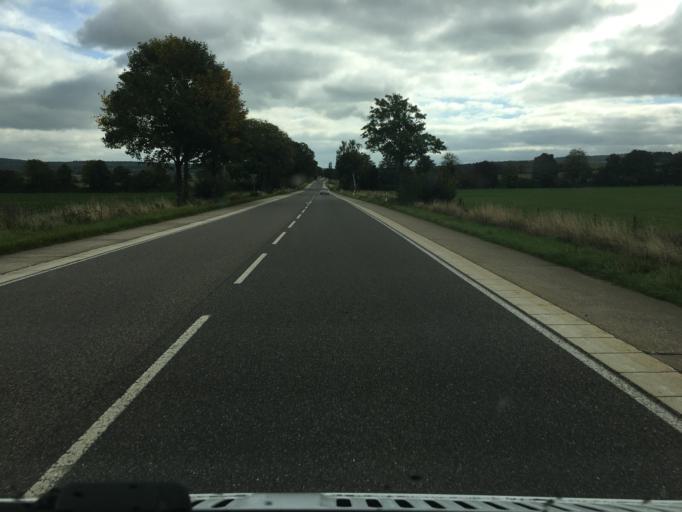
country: DE
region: North Rhine-Westphalia
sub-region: Regierungsbezirk Koln
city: Euskirchen
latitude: 50.6145
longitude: 6.8438
